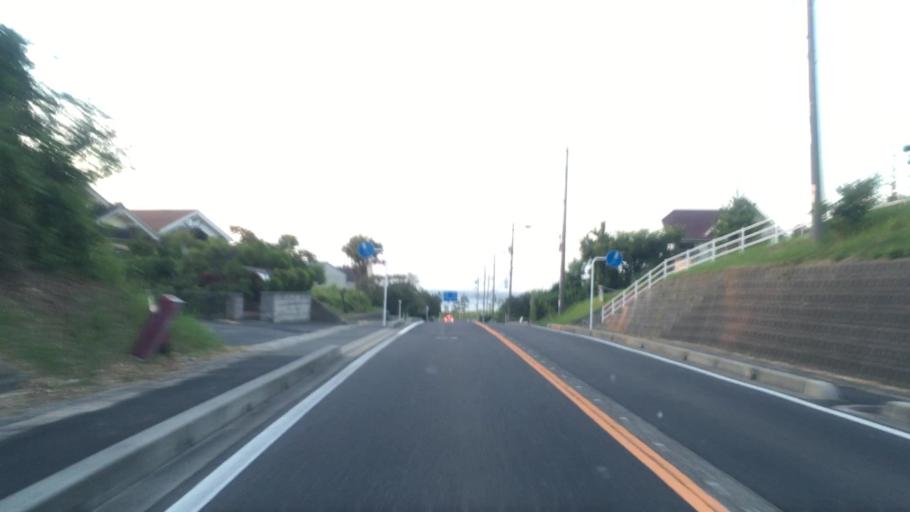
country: JP
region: Tottori
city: Tottori
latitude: 35.5885
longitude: 134.3326
